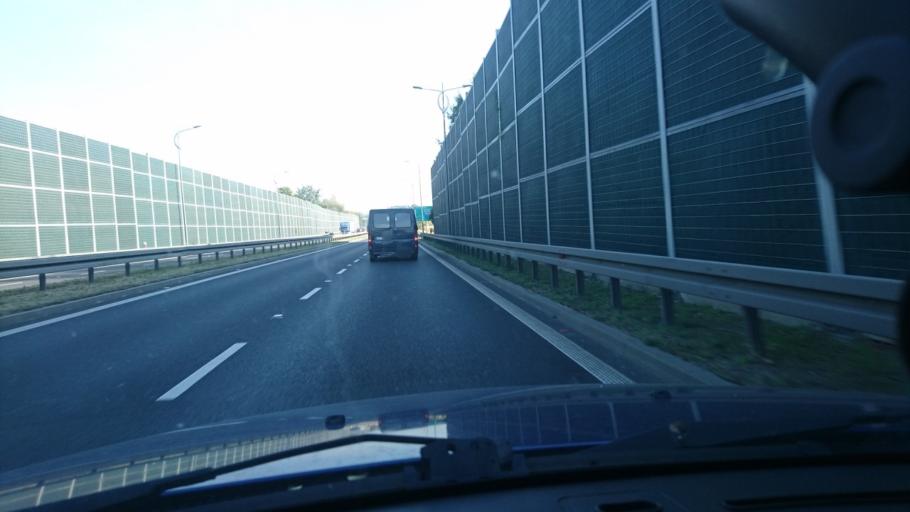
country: PL
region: Silesian Voivodeship
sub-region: Tychy
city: Cielmice
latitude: 50.1174
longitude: 19.0136
